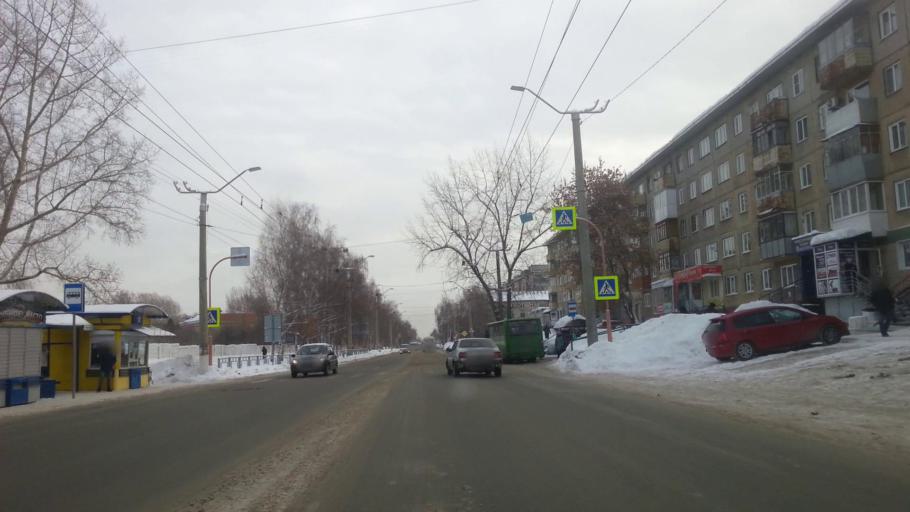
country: RU
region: Altai Krai
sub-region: Gorod Barnaulskiy
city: Barnaul
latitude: 53.3674
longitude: 83.7086
